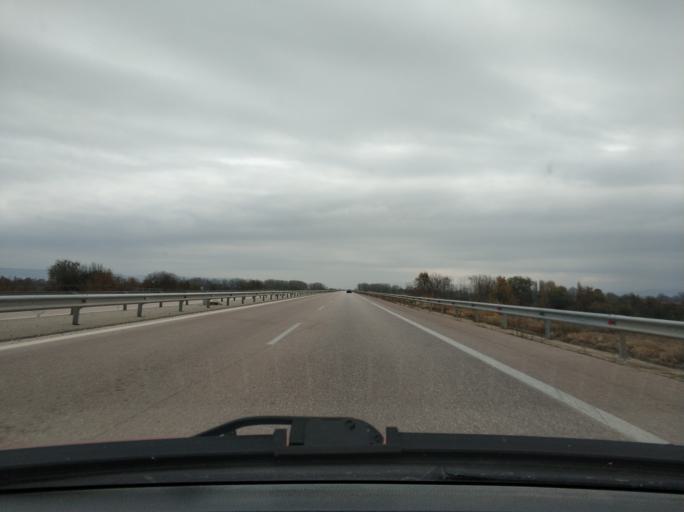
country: GR
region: Central Macedonia
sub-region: Nomos Thessalonikis
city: Kavallari
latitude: 40.7325
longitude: 23.0488
